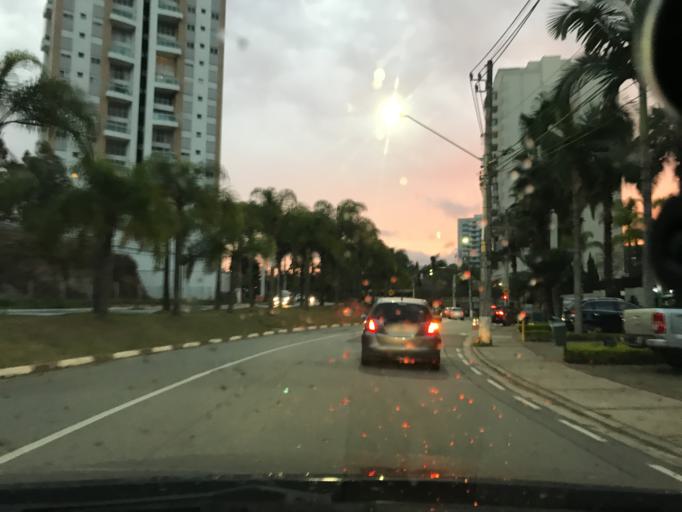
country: BR
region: Sao Paulo
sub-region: Barueri
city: Barueri
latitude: -23.4638
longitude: -46.8637
